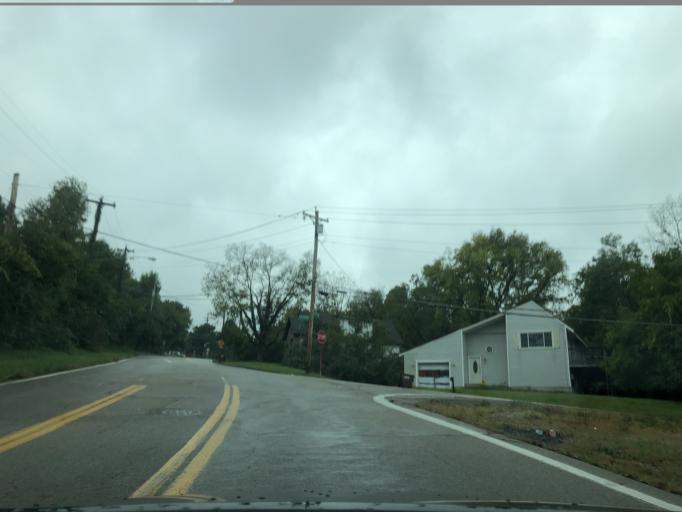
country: US
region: Ohio
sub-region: Hamilton County
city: Elmwood Place
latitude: 39.2042
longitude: -84.4963
